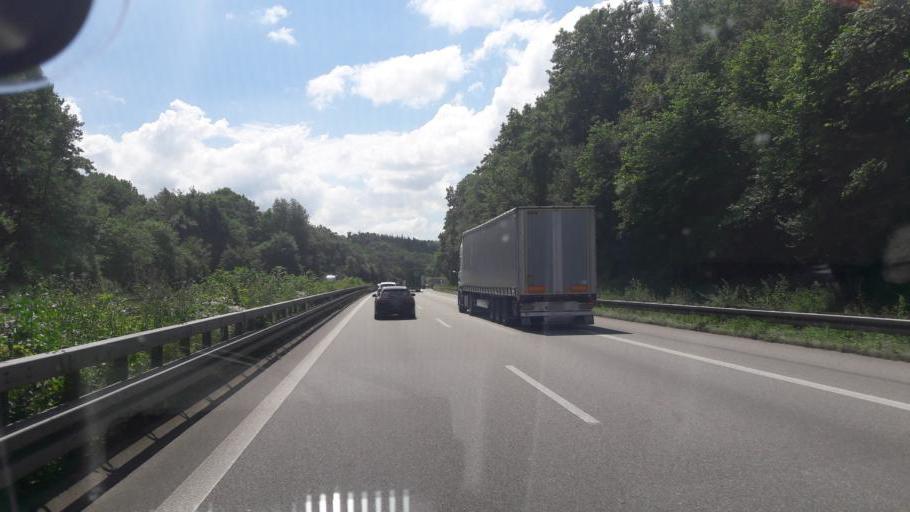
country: DE
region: Baden-Wuerttemberg
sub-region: Regierungsbezirk Stuttgart
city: Eberstadt
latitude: 49.1681
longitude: 9.3761
